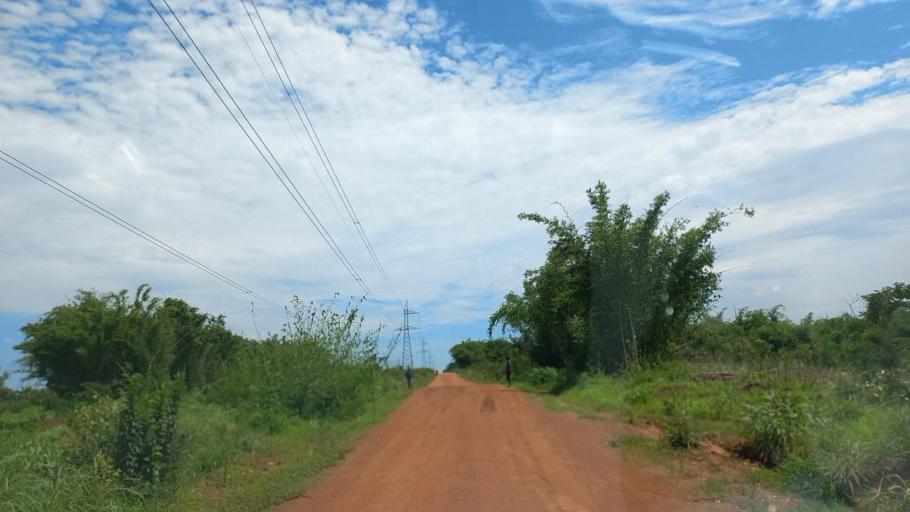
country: ZM
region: Copperbelt
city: Kitwe
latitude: -12.8048
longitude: 28.3632
